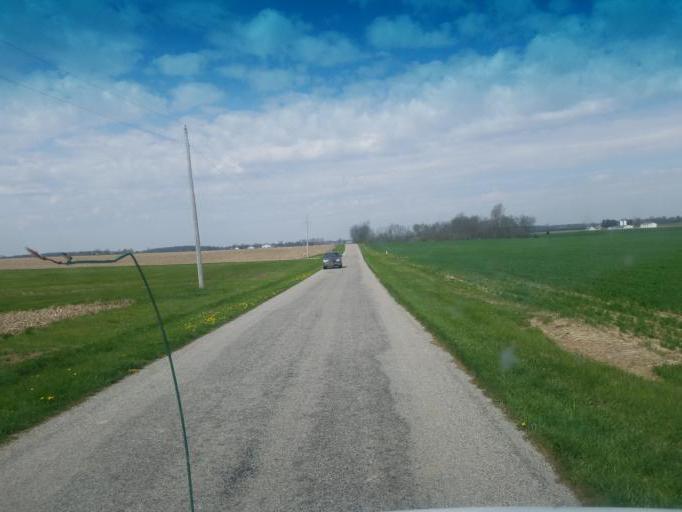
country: US
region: Ohio
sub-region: Logan County
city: Northwood
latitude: 40.4895
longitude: -83.7511
